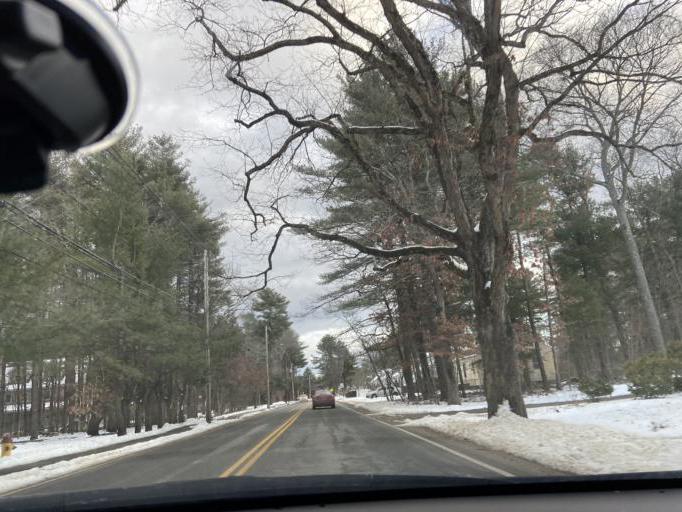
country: US
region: Massachusetts
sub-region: Norfolk County
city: Sharon
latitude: 42.1074
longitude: -71.2075
